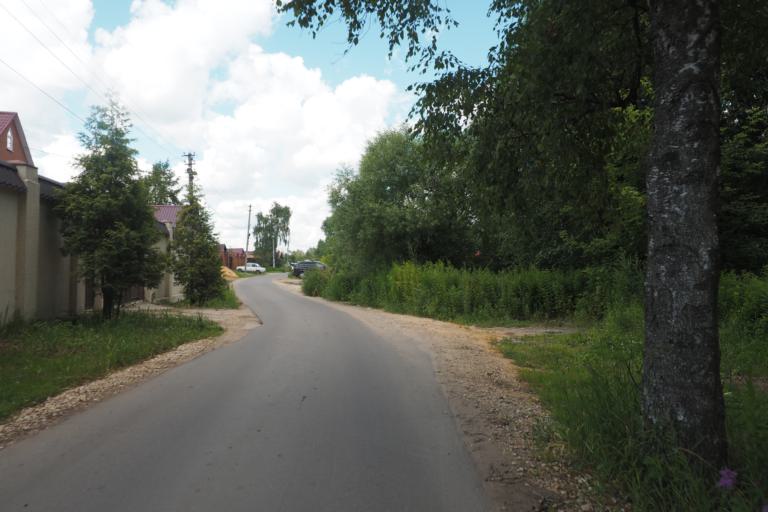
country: RU
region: Moskovskaya
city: Ramenskoye
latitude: 55.5829
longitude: 38.2547
